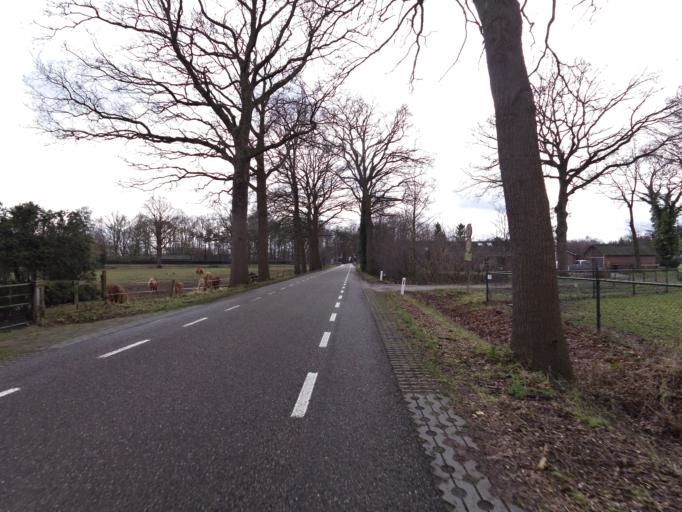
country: NL
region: Gelderland
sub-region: Oude IJsselstreek
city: Wisch
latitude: 51.9289
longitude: 6.4090
